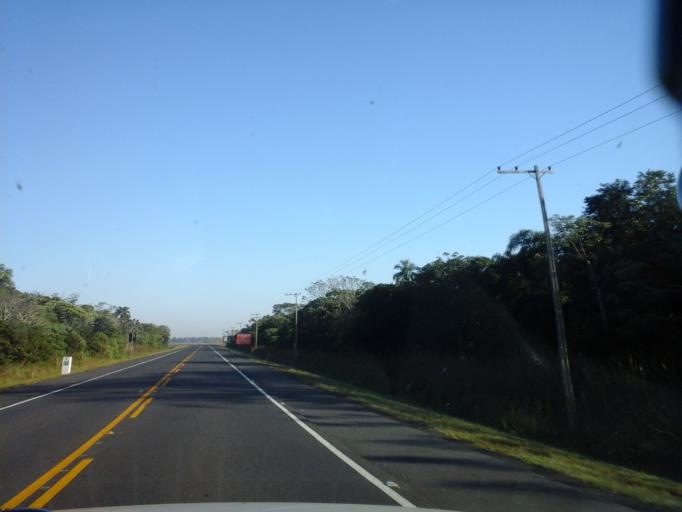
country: PY
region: Neembucu
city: Pilar
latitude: -26.8580
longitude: -57.9582
